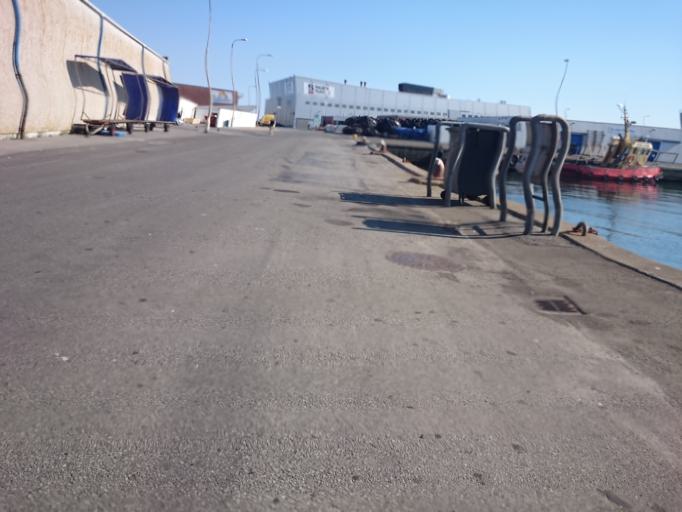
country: DK
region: North Denmark
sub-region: Frederikshavn Kommune
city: Skagen
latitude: 57.7207
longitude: 10.5949
